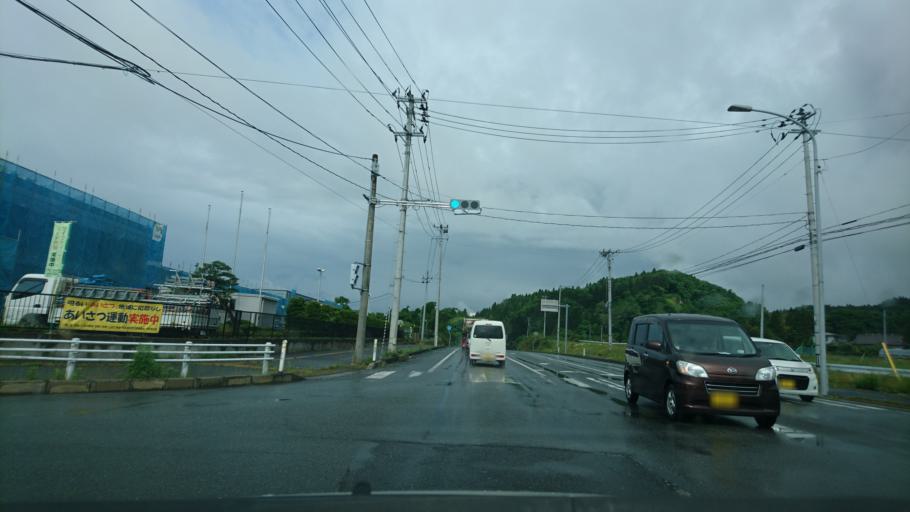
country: JP
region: Iwate
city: Ichinoseki
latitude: 38.9410
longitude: 141.0828
